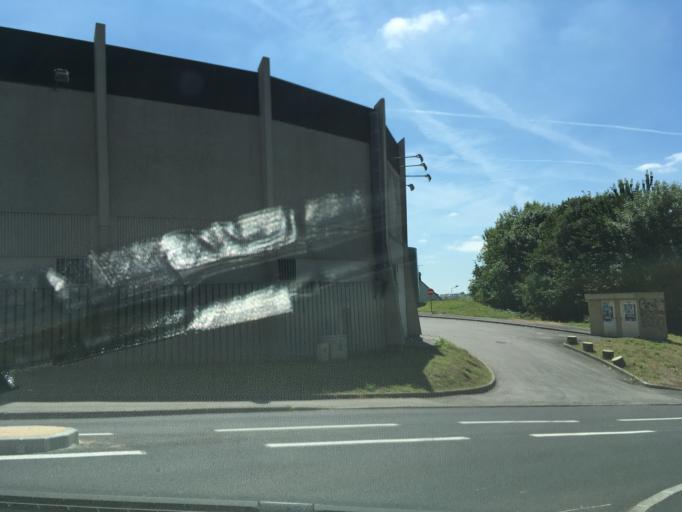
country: FR
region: Brittany
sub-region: Departement du Finistere
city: Quimper
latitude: 48.0093
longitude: -4.1064
